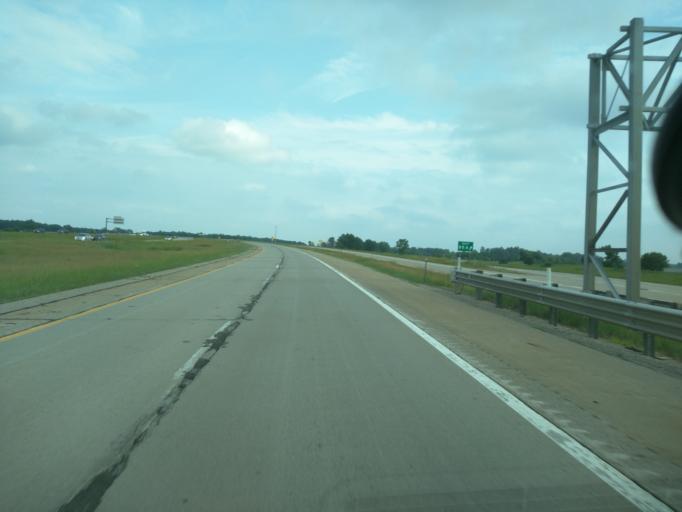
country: US
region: Michigan
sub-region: Clinton County
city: DeWitt
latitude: 42.8103
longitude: -84.5163
